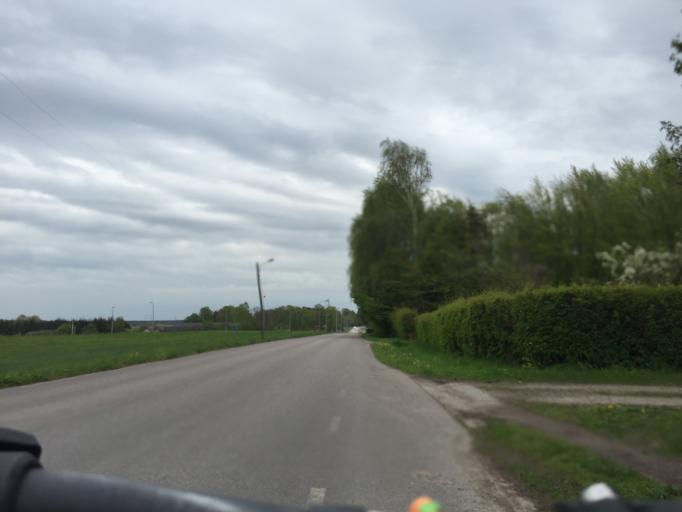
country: SE
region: Skane
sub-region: Lunds Kommun
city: Veberod
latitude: 55.6449
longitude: 13.4689
